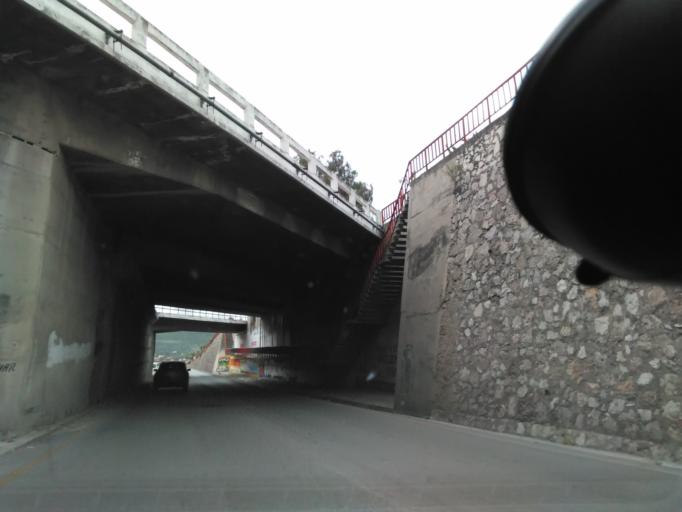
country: MX
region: Hidalgo
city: El Llano
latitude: 20.0547
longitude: -99.3188
